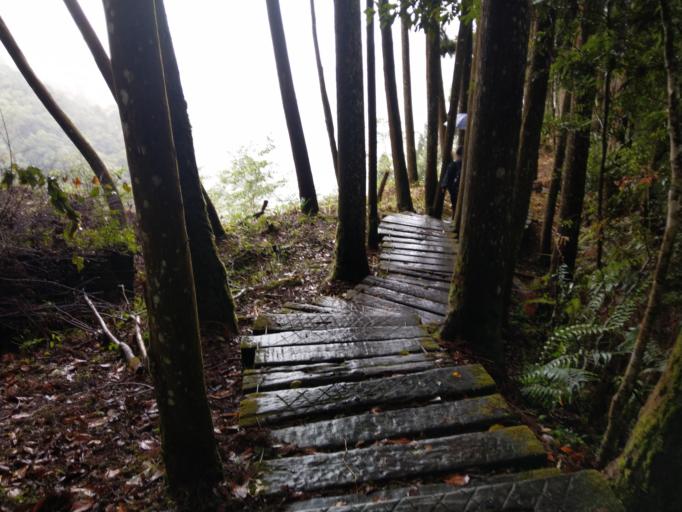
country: TW
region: Taiwan
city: Lugu
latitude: 23.6376
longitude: 120.7833
